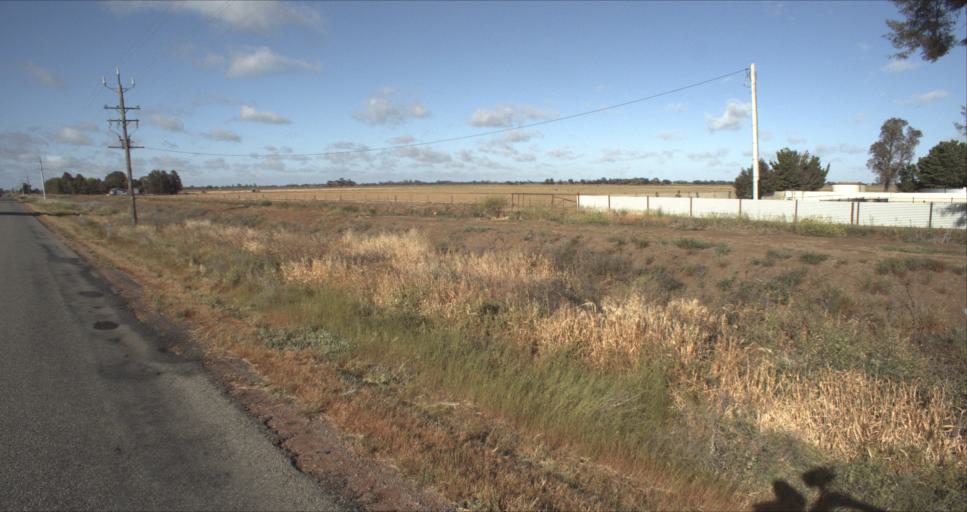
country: AU
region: New South Wales
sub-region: Leeton
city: Leeton
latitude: -34.5177
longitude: 146.3912
